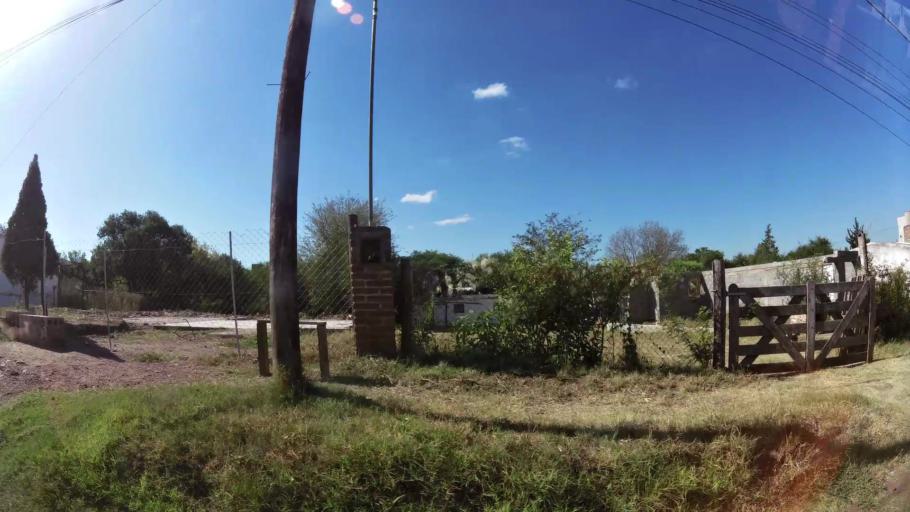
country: AR
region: Cordoba
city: La Calera
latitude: -31.3522
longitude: -64.3131
